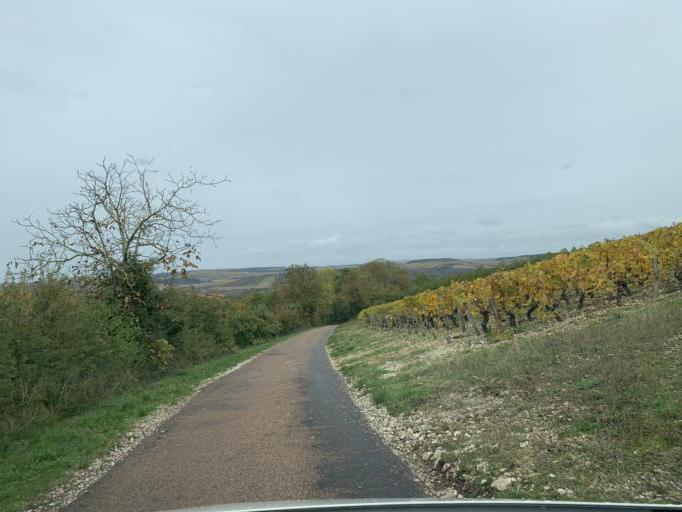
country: FR
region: Bourgogne
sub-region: Departement de l'Yonne
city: Champs-sur-Yonne
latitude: 47.7164
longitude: 3.5752
